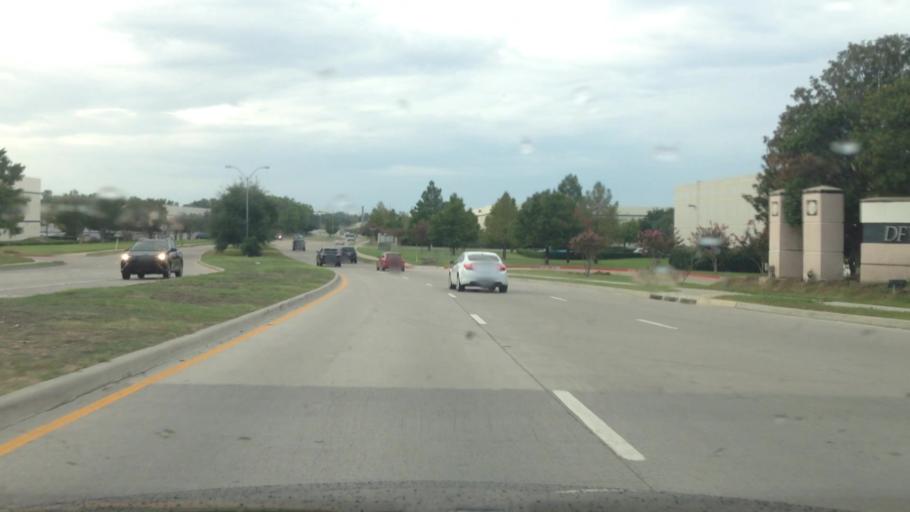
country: US
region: Texas
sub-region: Dallas County
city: Coppell
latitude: 32.9811
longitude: -97.0211
